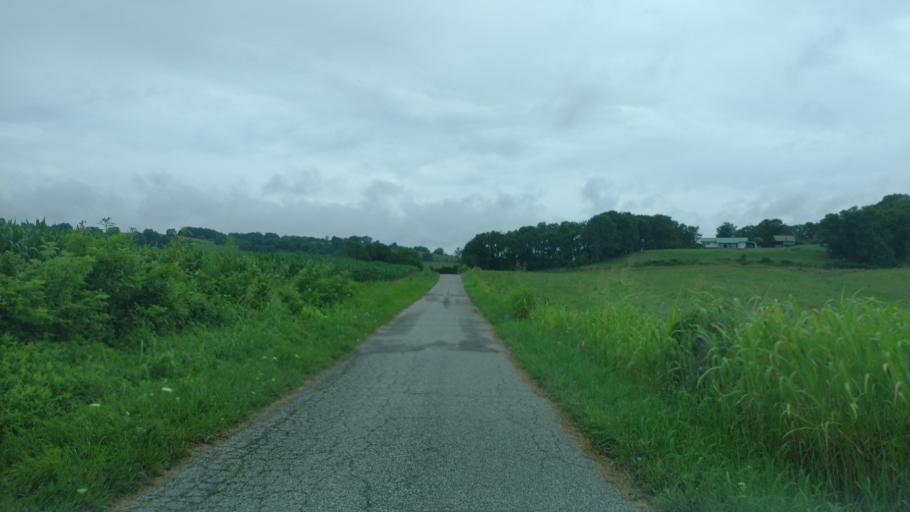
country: US
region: West Virginia
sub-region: Mason County
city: New Haven
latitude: 38.9243
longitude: -81.9519
